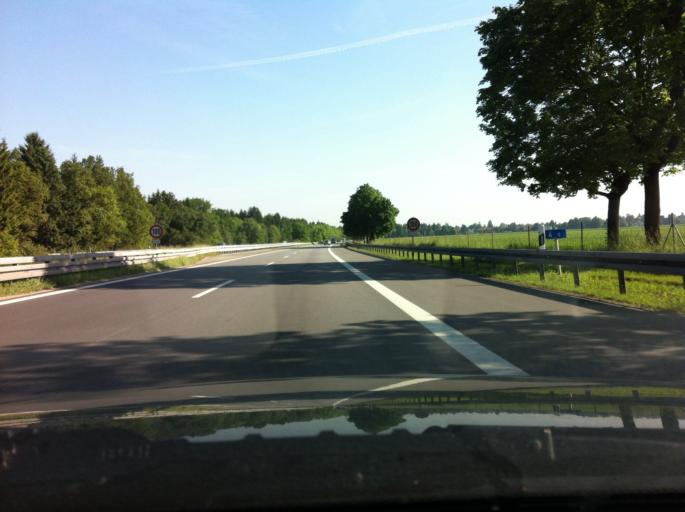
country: DE
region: Bavaria
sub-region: Upper Bavaria
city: Unterhaching
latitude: 48.0596
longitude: 11.5952
